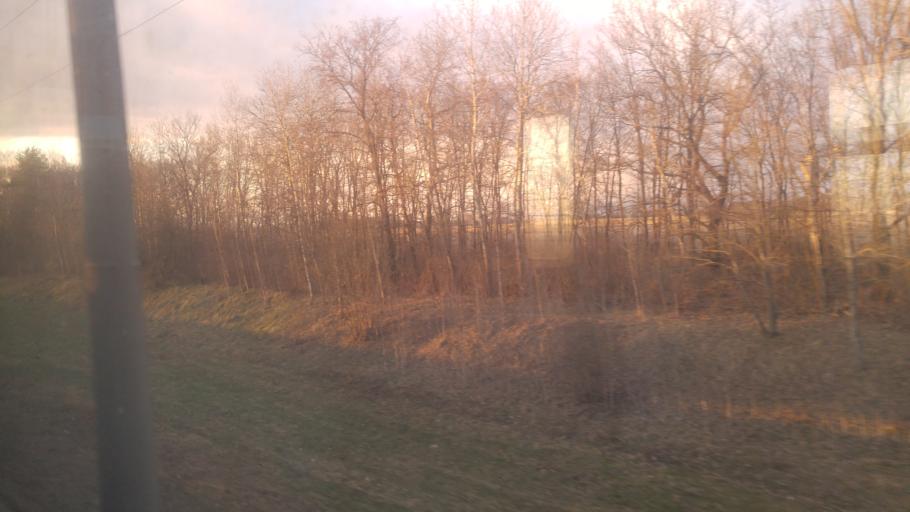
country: BY
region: Minsk
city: Rudzyensk
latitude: 53.6475
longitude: 27.7813
